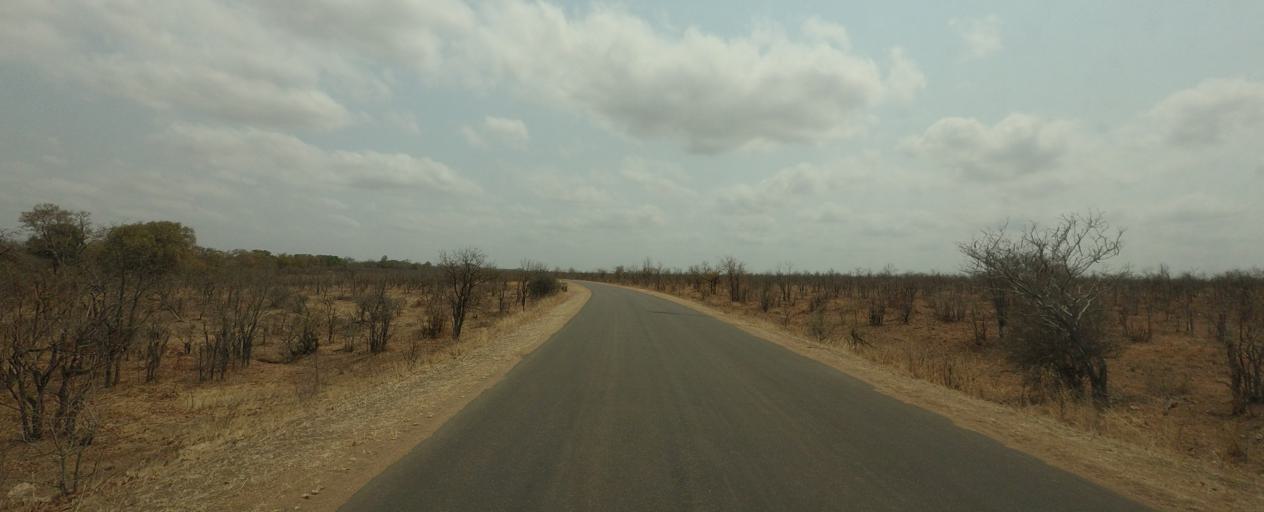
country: ZA
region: Limpopo
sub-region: Mopani District Municipality
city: Phalaborwa
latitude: -23.5434
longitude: 31.4276
